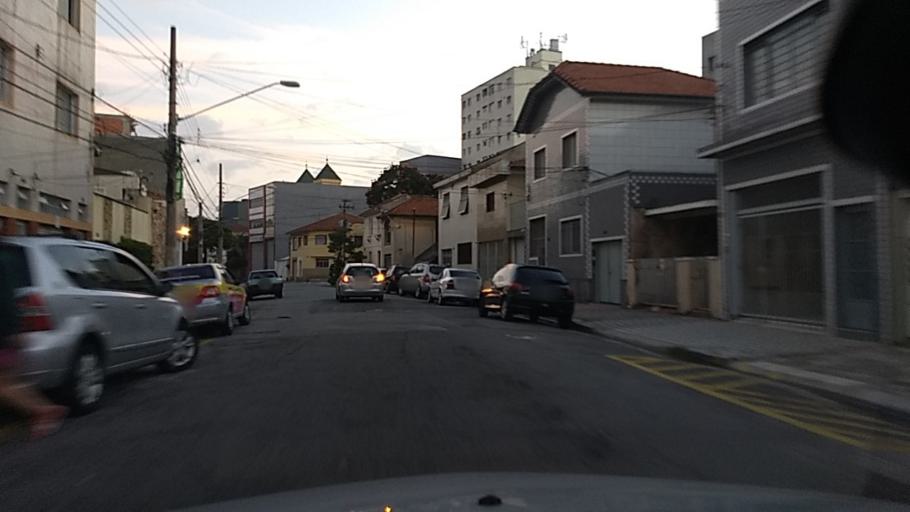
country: BR
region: Sao Paulo
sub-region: Sao Paulo
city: Sao Paulo
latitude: -23.5302
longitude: -46.6171
